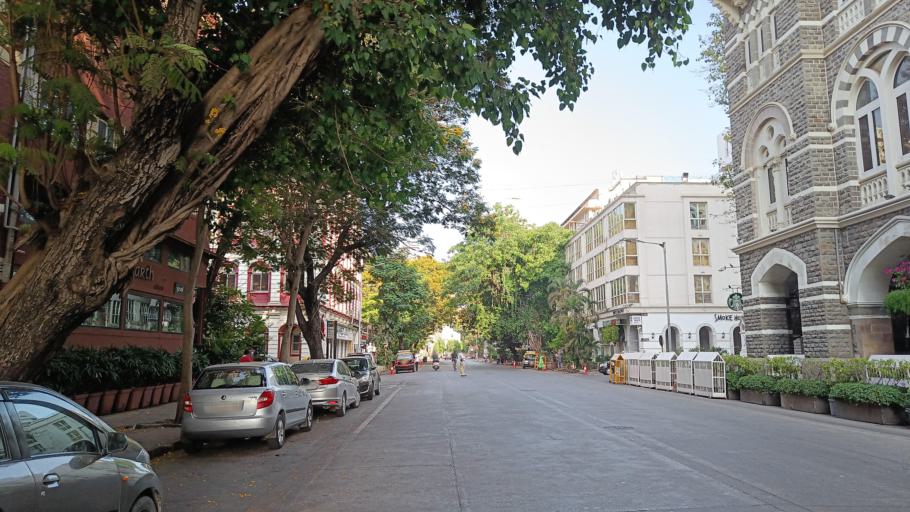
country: IN
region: Maharashtra
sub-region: Raigarh
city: Uran
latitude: 18.9213
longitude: 72.8328
